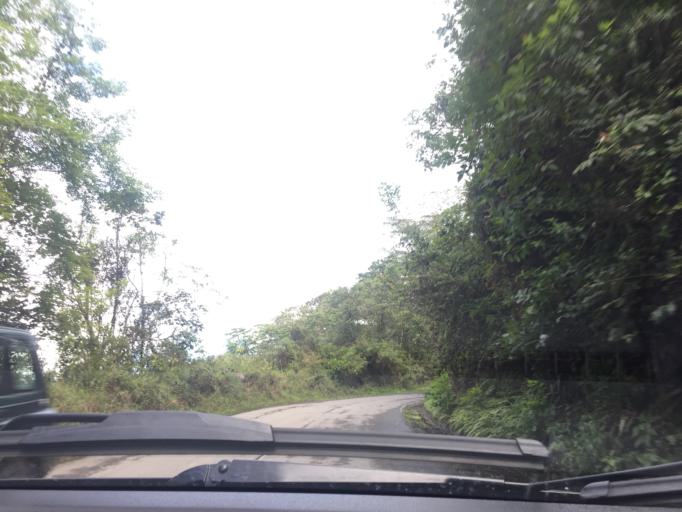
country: CO
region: Cundinamarca
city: Supata
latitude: 5.0282
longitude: -74.2730
